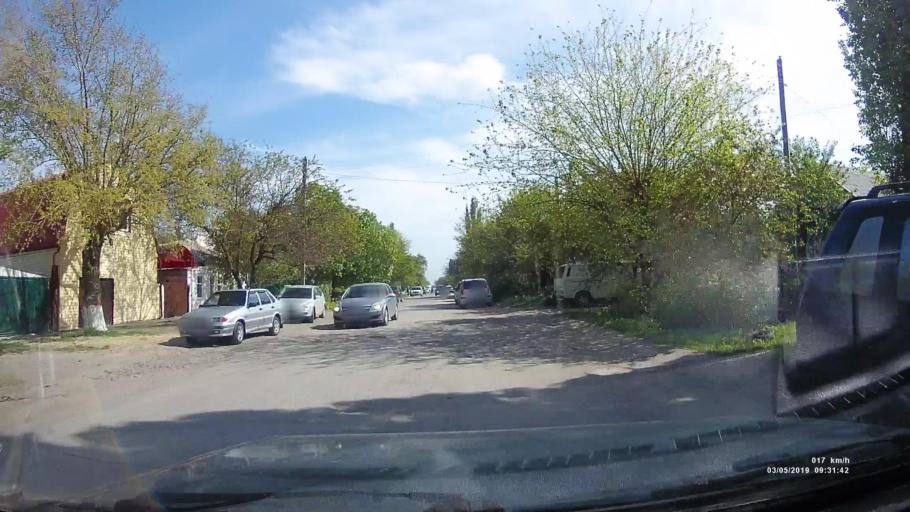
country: RU
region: Rostov
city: Azov
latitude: 47.1005
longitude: 39.4275
